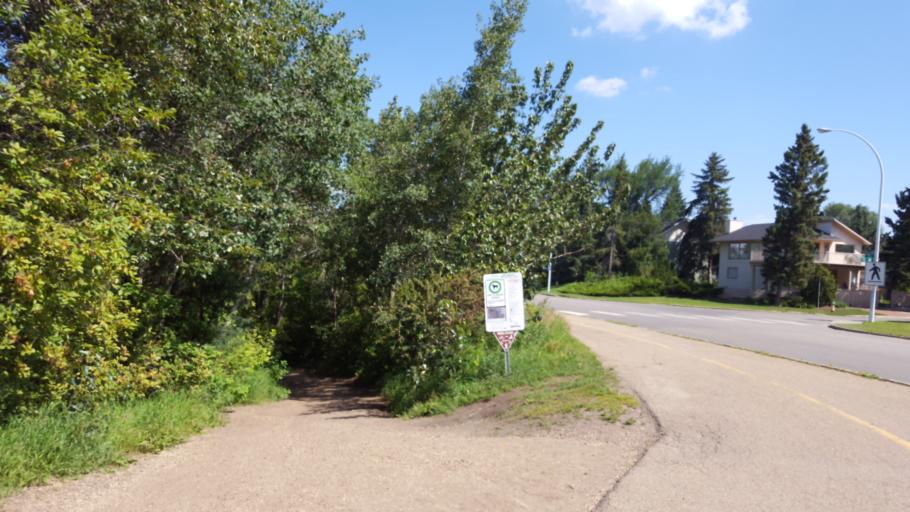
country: CA
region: Alberta
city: Edmonton
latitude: 53.5123
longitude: -113.5390
